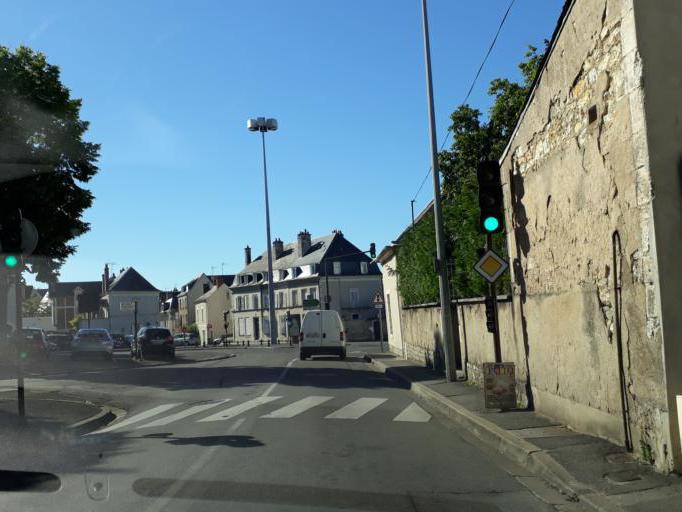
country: FR
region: Centre
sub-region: Departement du Cher
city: Bourges
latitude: 47.0838
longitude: 2.4032
